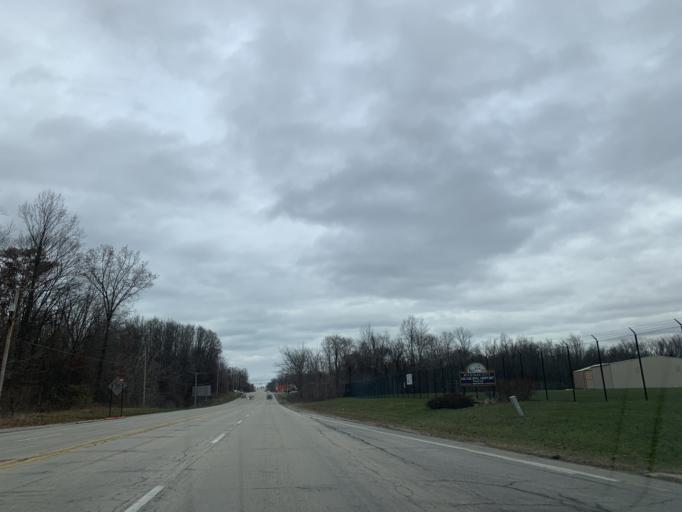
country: US
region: Indiana
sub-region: LaPorte County
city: Trail Creek
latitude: 41.7059
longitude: -86.8259
